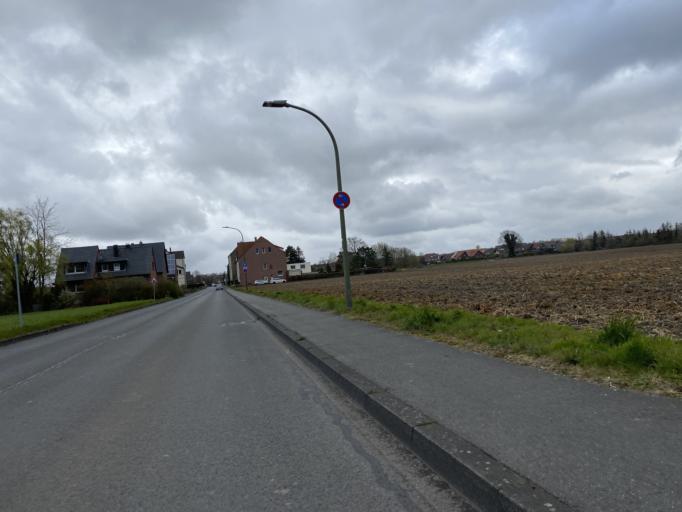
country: DE
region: North Rhine-Westphalia
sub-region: Regierungsbezirk Arnsberg
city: Hamm
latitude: 51.6815
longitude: 7.8923
